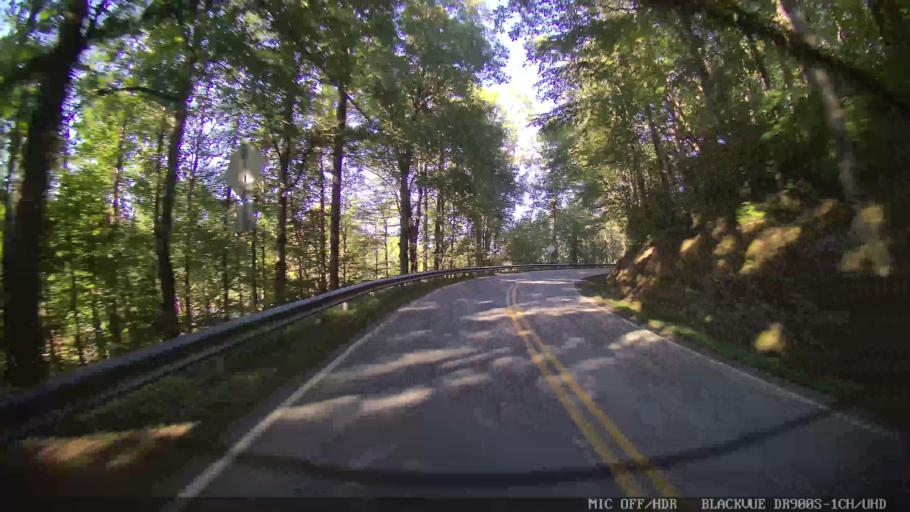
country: US
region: Georgia
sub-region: Lumpkin County
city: Dahlonega
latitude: 34.7031
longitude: -84.0527
